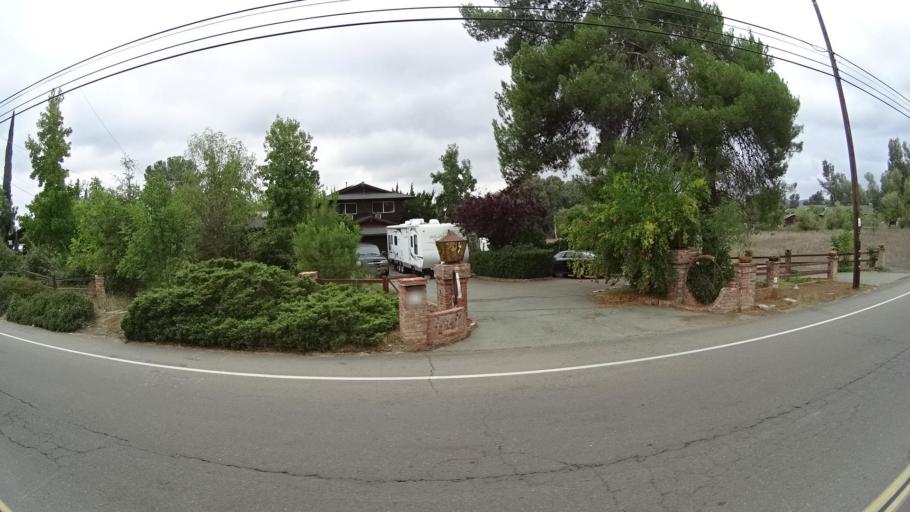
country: US
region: California
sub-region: San Diego County
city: Ramona
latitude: 33.0291
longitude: -116.8794
